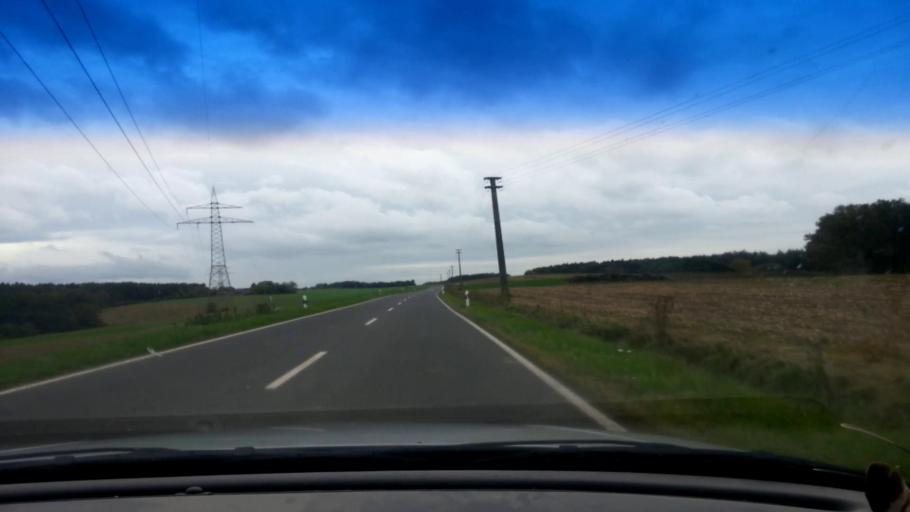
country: DE
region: Bavaria
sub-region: Regierungsbezirk Unterfranken
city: Kirchlauter
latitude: 50.0335
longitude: 10.7557
